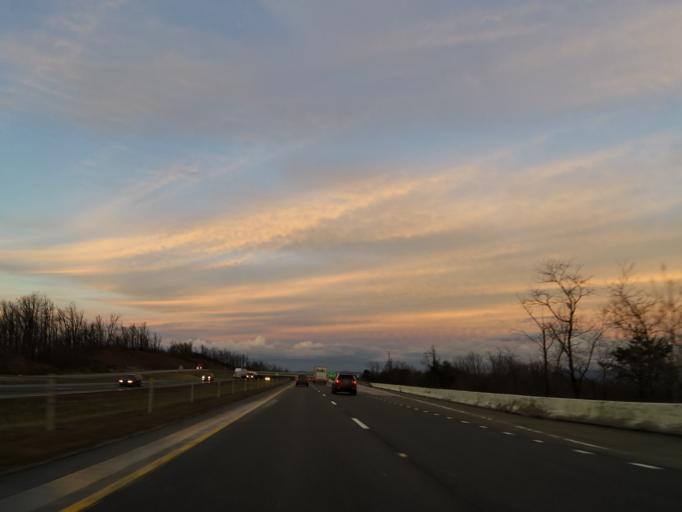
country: US
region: Tennessee
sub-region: Campbell County
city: Jellico
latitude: 36.5306
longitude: -84.1705
